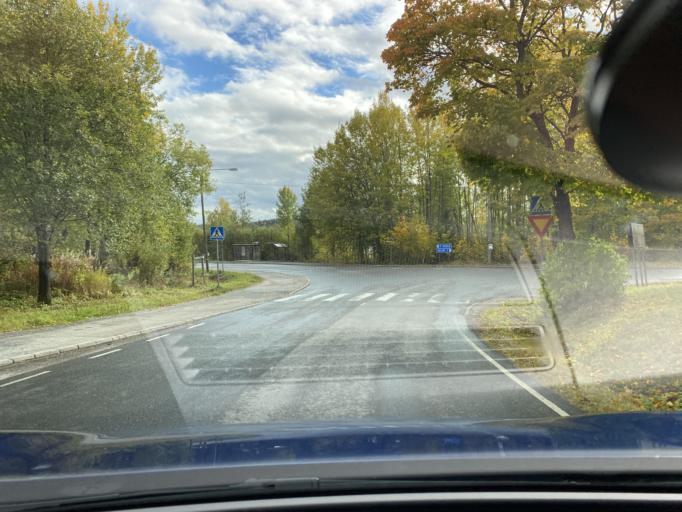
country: FI
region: Pirkanmaa
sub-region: Tampere
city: Nokia
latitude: 61.4757
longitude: 23.3437
